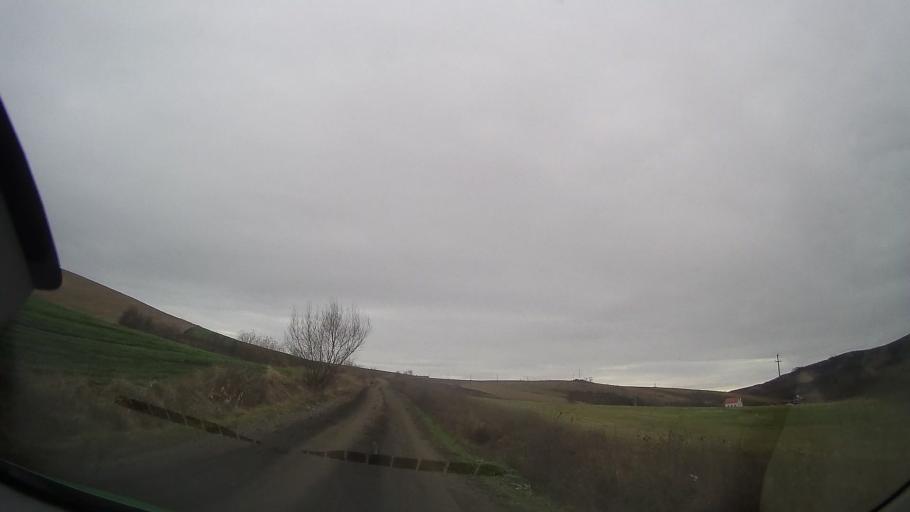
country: RO
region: Mures
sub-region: Comuna Bala
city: Bala
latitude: 46.6956
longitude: 24.4898
